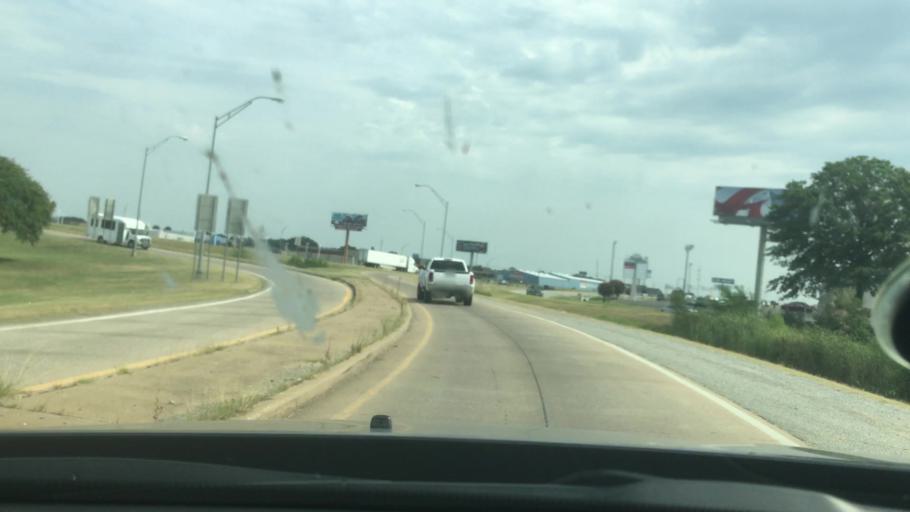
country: US
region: Oklahoma
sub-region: Bryan County
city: Durant
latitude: 33.9982
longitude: -96.4024
